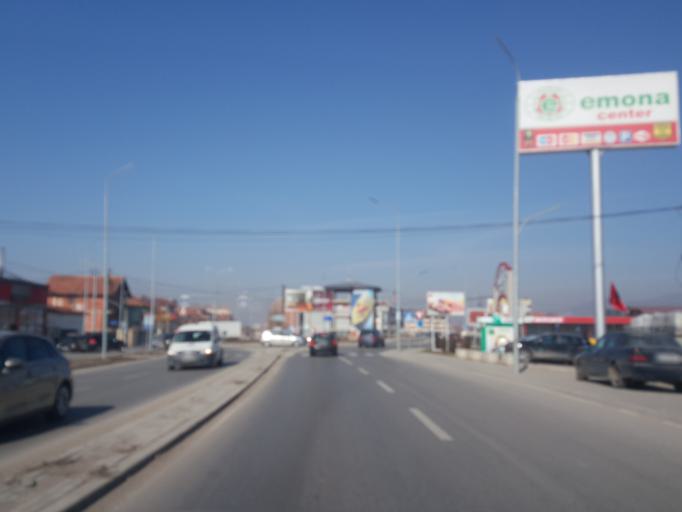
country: XK
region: Mitrovica
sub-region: Vushtrri
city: Vushtrri
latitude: 42.8145
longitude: 20.9837
